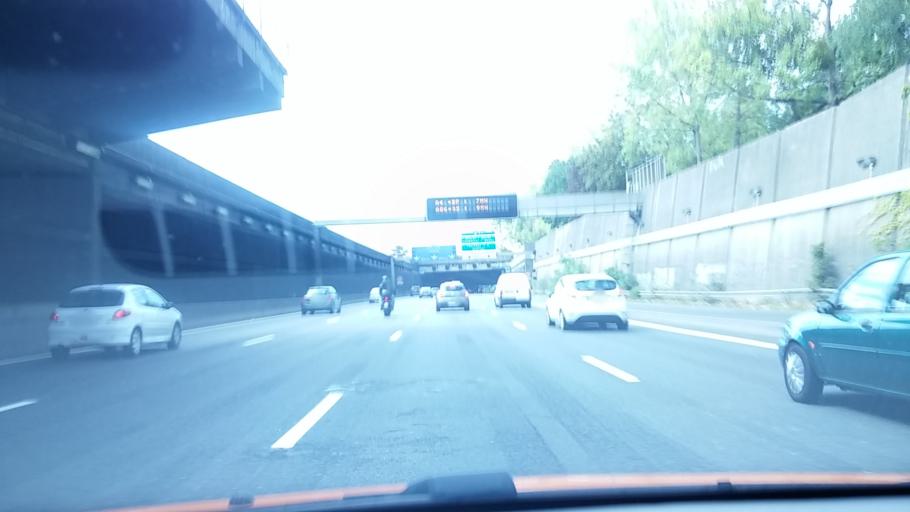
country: FR
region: Ile-de-France
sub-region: Departement du Val-de-Marne
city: Champigny-sur-Marne
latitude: 48.8274
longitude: 2.5070
